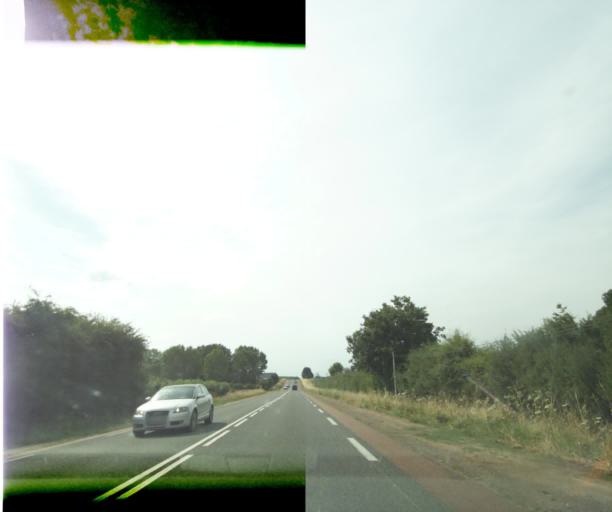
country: FR
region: Pays de la Loire
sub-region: Departement de la Sarthe
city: Luceau
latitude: 47.7414
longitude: 0.3868
